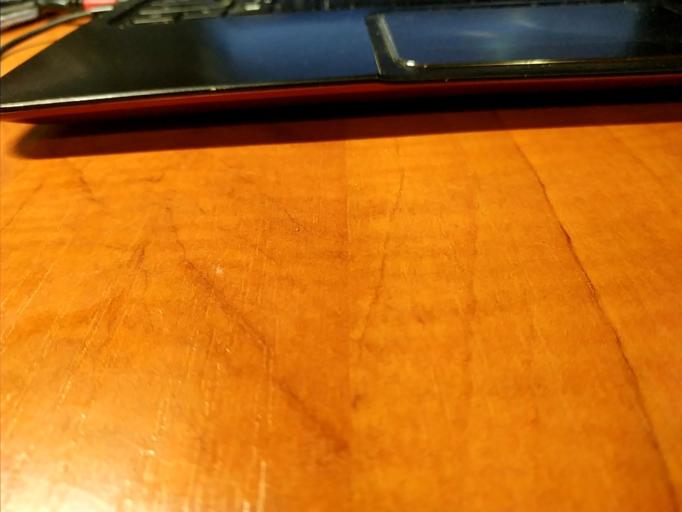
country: RU
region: Tverskaya
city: Ves'yegonsk
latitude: 58.8145
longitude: 37.5435
